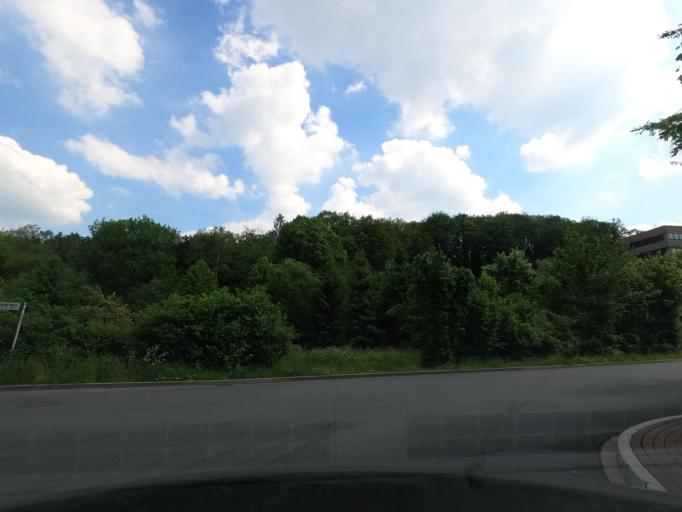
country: DE
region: North Rhine-Westphalia
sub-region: Regierungsbezirk Arnsberg
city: Luedenscheid
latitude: 51.2502
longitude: 7.6006
